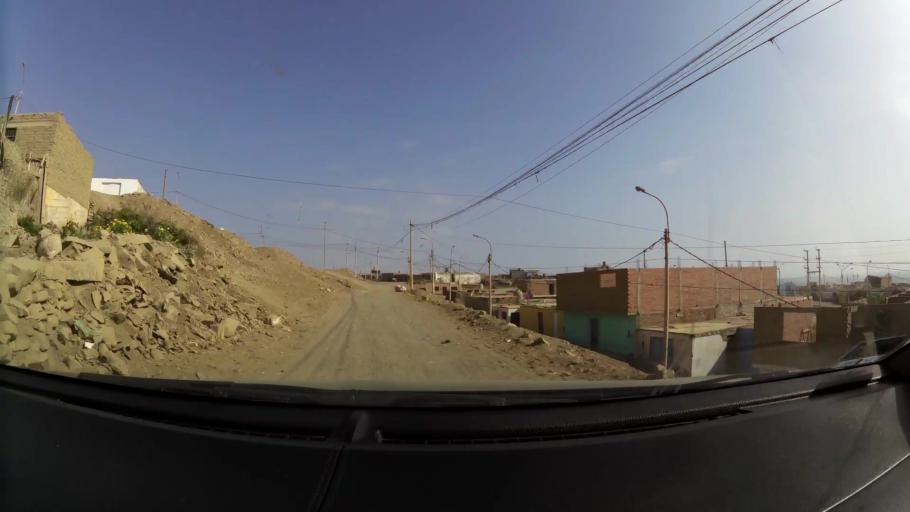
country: PE
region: Lima
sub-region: Huaura
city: Huacho
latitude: -11.1292
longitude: -77.6158
